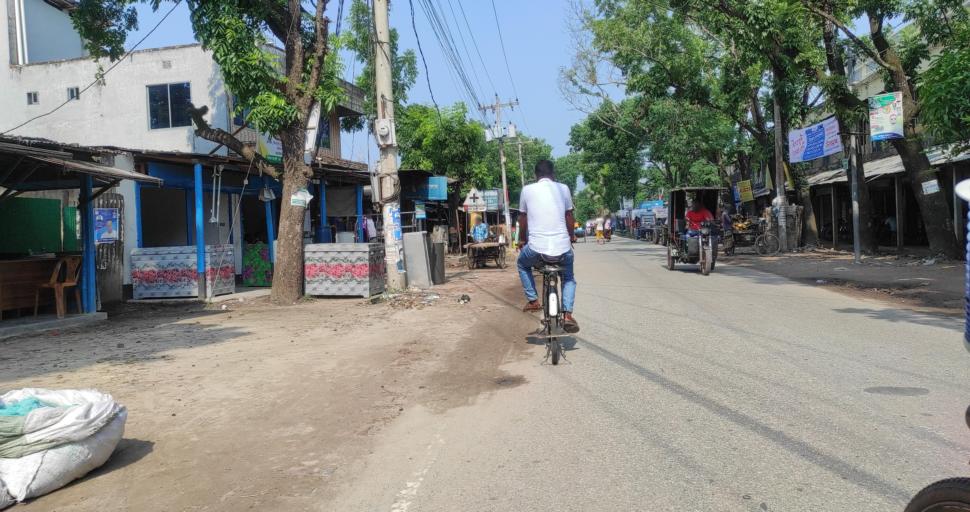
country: BD
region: Rajshahi
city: Ishurdi
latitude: 24.2900
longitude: 89.0775
